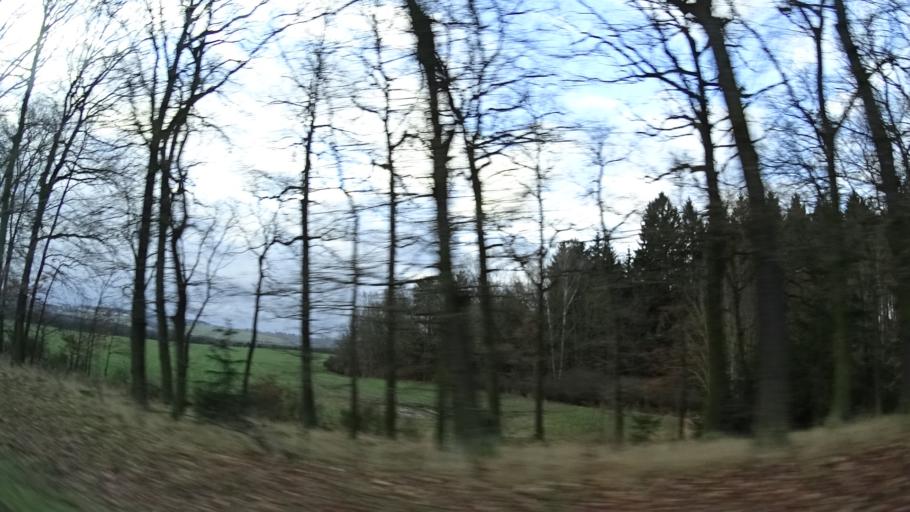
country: DE
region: Thuringia
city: Zeulenroda
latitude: 50.6690
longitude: 11.9555
